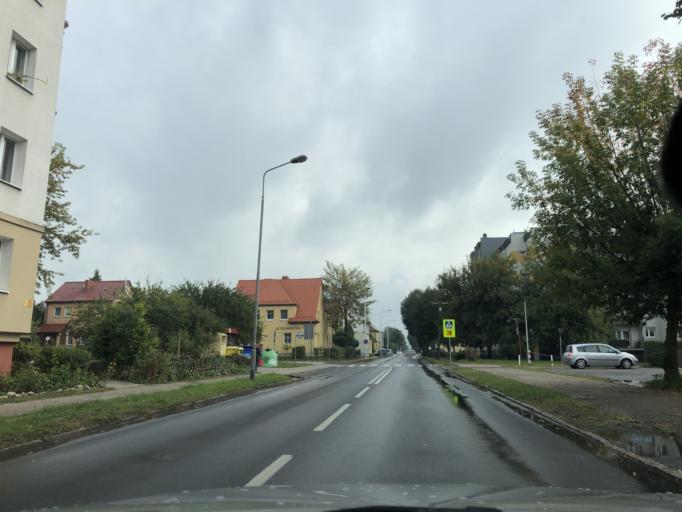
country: PL
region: Greater Poland Voivodeship
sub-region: Powiat pilski
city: Pila
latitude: 53.1512
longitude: 16.7593
